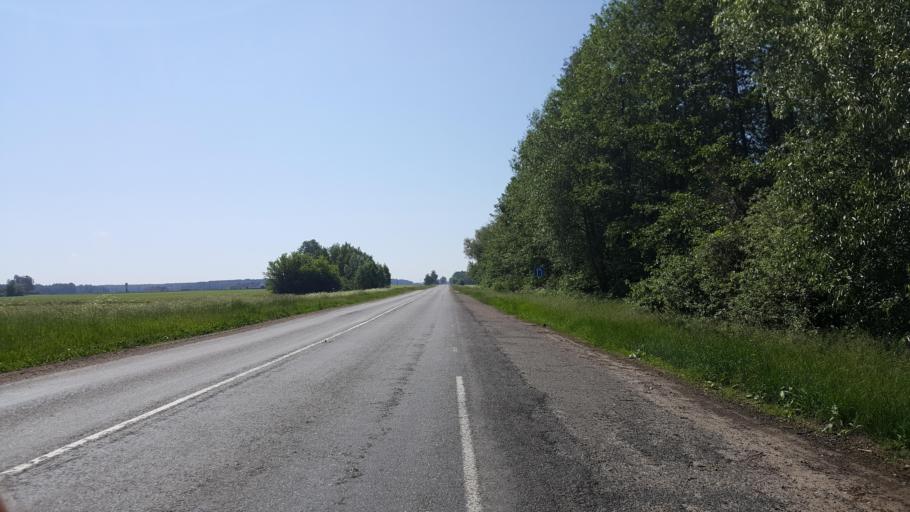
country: BY
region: Brest
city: Zhabinka
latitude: 52.2638
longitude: 23.9603
